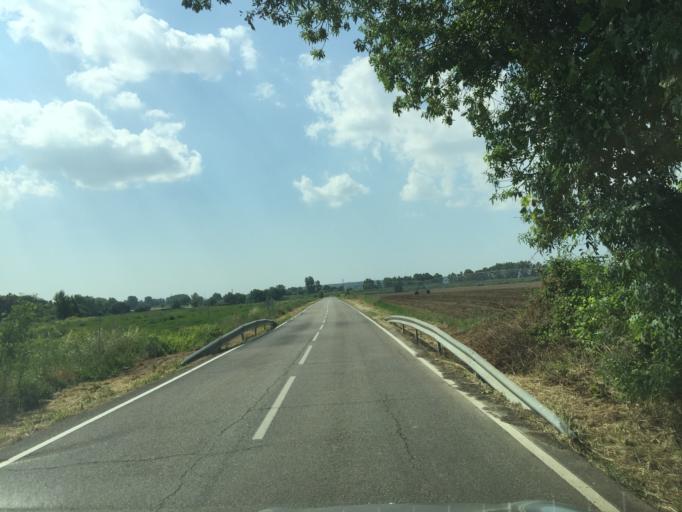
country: PT
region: Santarem
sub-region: Alpiarca
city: Alpiarca
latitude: 39.2996
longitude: -8.5564
